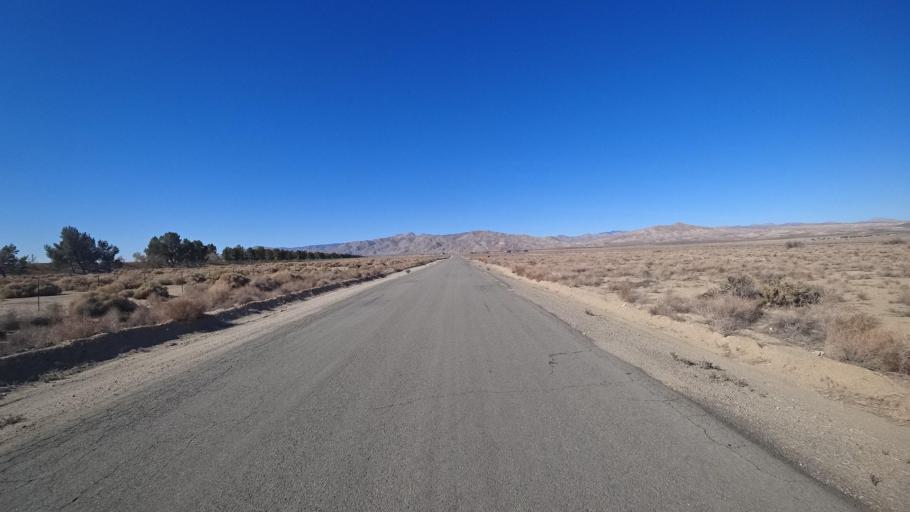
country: US
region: California
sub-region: Kern County
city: California City
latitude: 35.2868
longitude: -117.9521
